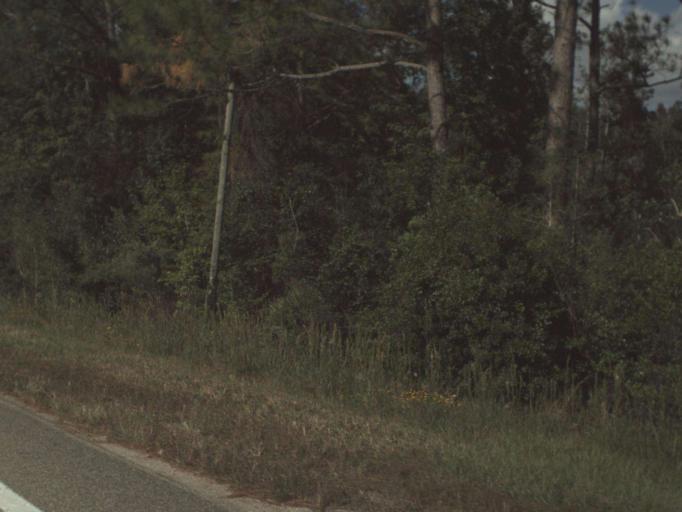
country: US
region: Florida
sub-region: Leon County
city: Woodville
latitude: 30.2211
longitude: -84.2015
